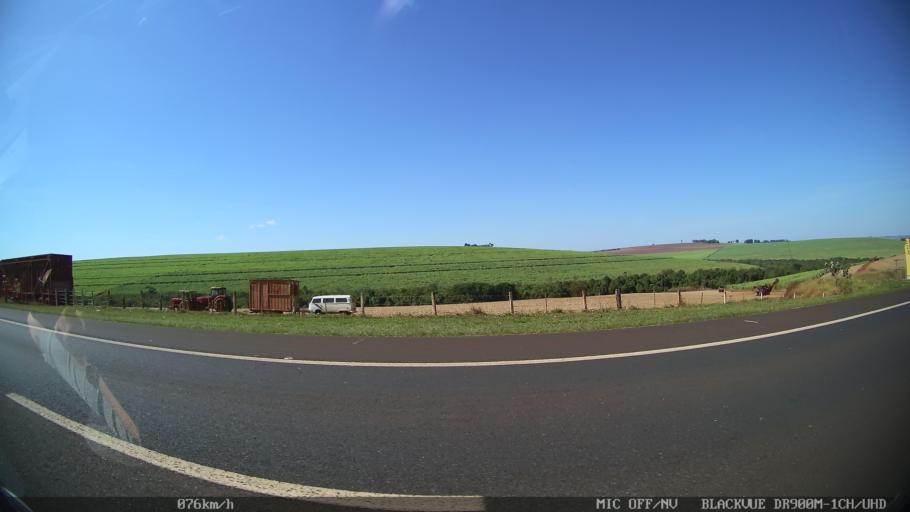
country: BR
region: Sao Paulo
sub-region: Batatais
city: Batatais
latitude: -20.7098
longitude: -47.5045
